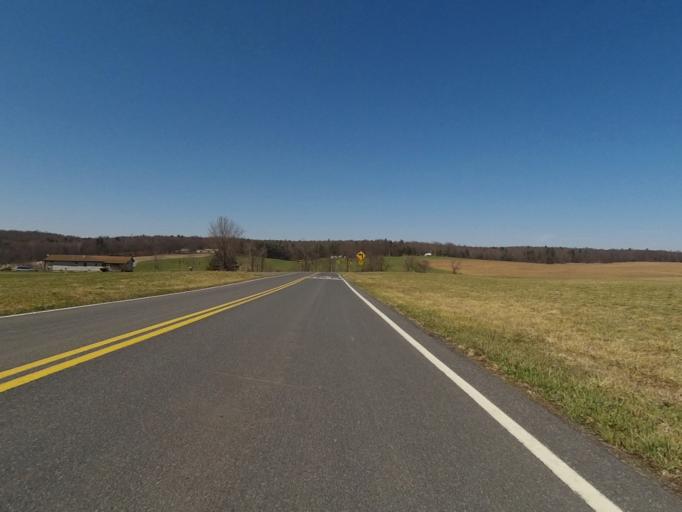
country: US
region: Pennsylvania
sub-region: Centre County
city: Stormstown
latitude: 40.7480
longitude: -78.0071
